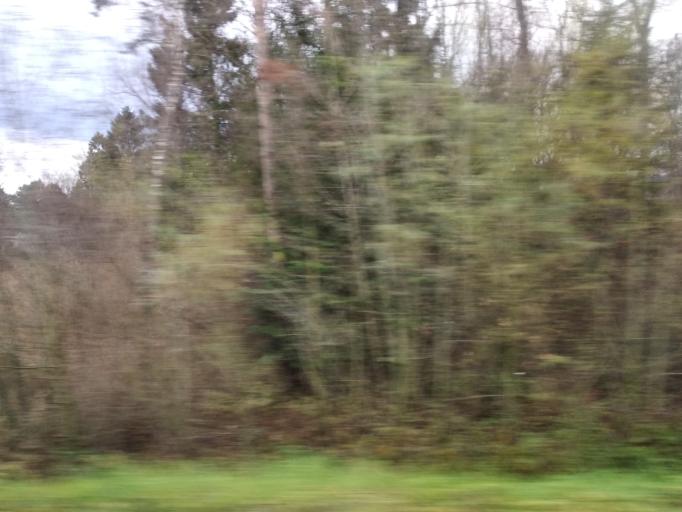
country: AT
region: Vorarlberg
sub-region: Politischer Bezirk Dornbirn
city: Hohenems
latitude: 47.3776
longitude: 9.6712
